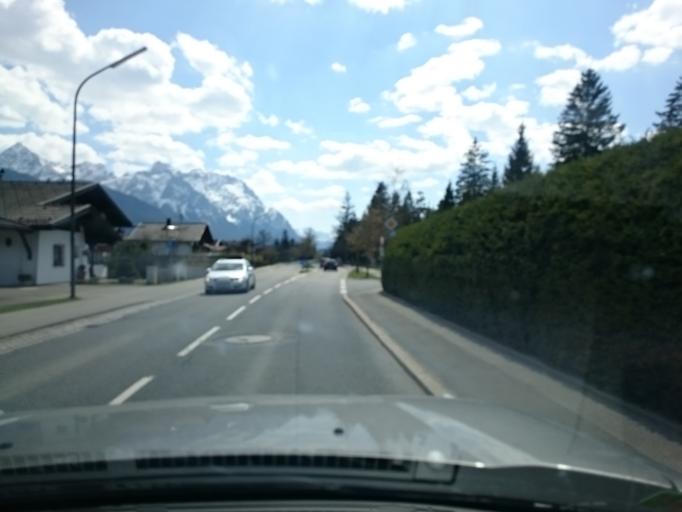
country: DE
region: Bavaria
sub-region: Upper Bavaria
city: Krun
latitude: 47.5012
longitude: 11.2781
